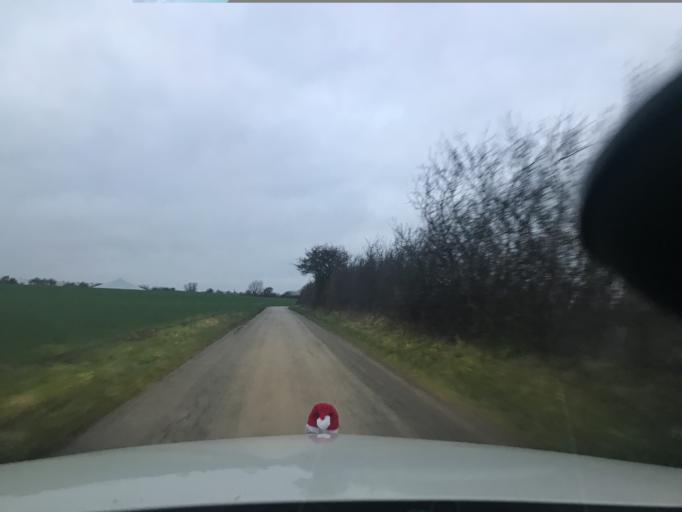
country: DK
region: South Denmark
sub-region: Sonderborg Kommune
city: Dybbol
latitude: 54.8510
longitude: 9.7355
